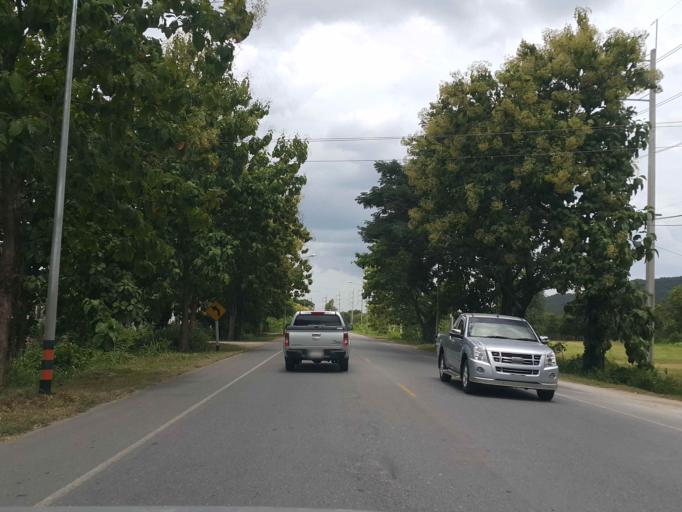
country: TH
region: Lamphun
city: Pa Sang
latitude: 18.4564
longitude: 98.9085
